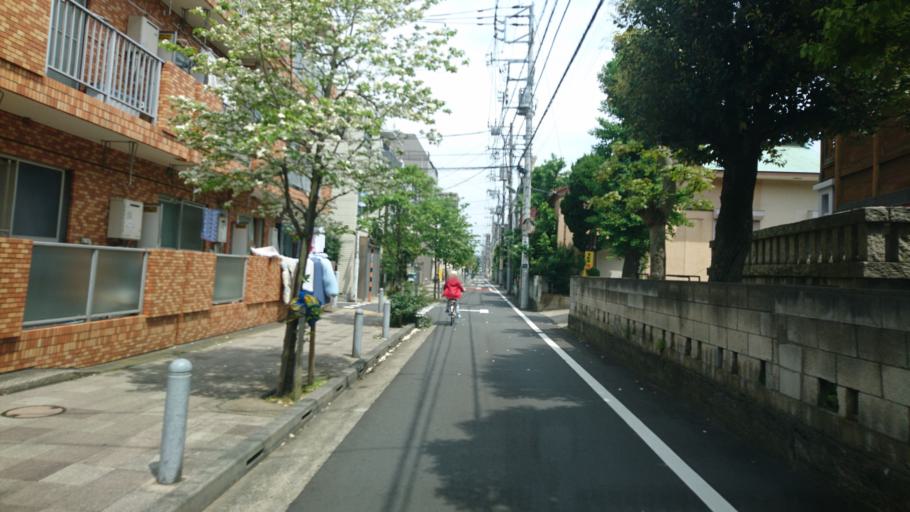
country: JP
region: Kanagawa
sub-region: Kawasaki-shi
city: Kawasaki
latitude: 35.5759
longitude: 139.7297
